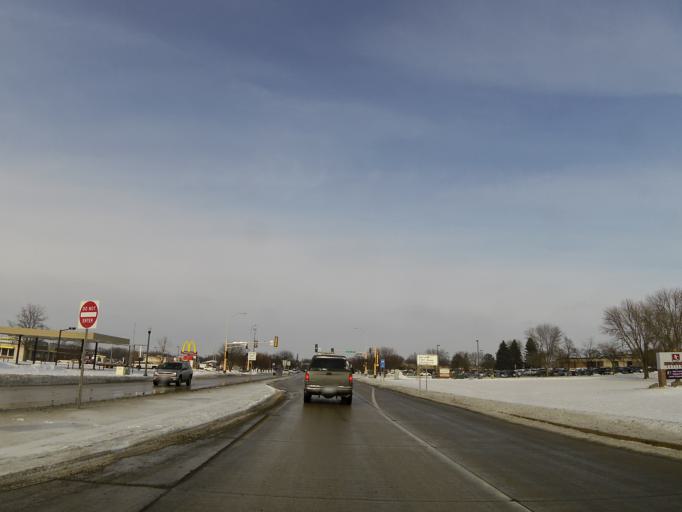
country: US
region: Minnesota
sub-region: McLeod County
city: Hutchinson
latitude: 44.8739
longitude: -94.3755
